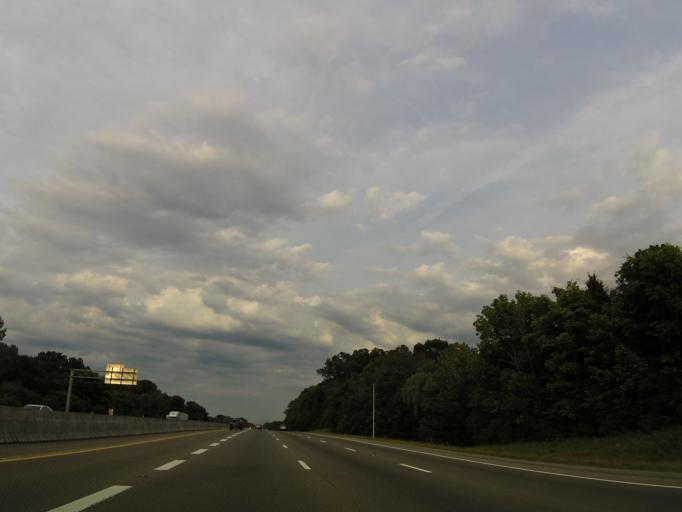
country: US
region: Tennessee
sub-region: Wilson County
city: Green Hill
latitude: 36.1690
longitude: -86.5790
